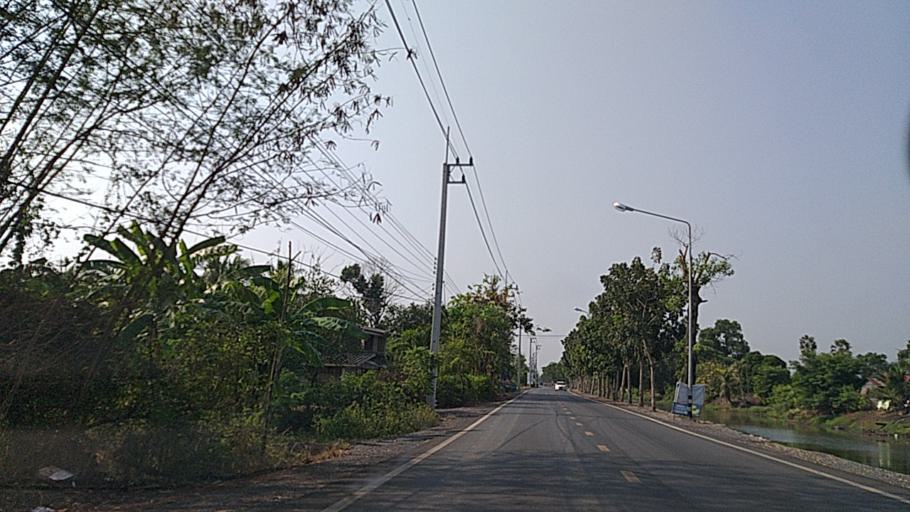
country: TH
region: Pathum Thani
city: Thanyaburi
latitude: 13.9853
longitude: 100.7059
